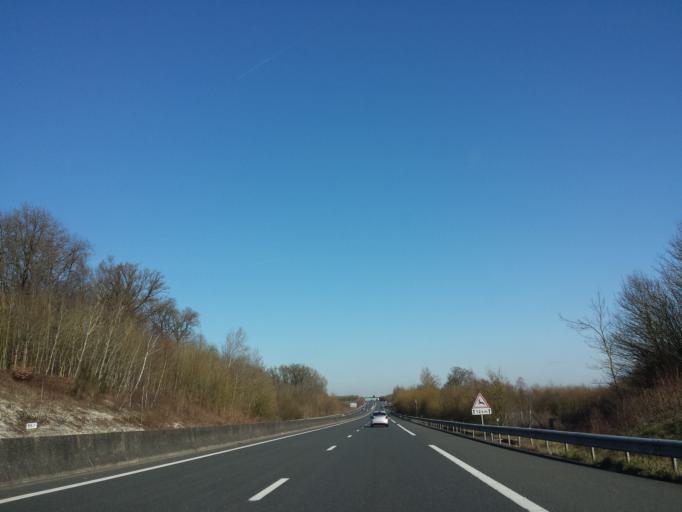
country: FR
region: Picardie
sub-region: Departement de l'Oise
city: Tille
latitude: 49.5454
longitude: 2.1882
